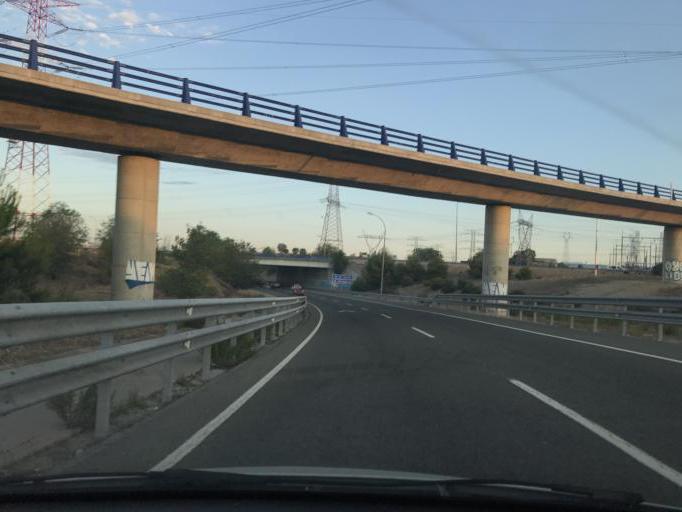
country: ES
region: Madrid
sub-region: Provincia de Madrid
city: San Sebastian de los Reyes
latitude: 40.5619
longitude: -3.5932
